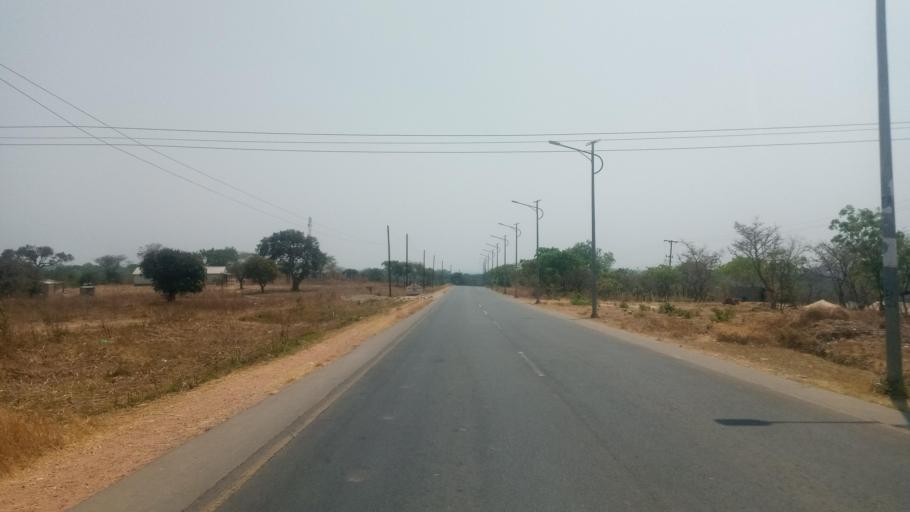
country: ZM
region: Lusaka
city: Lusaka
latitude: -15.4645
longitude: 28.4326
